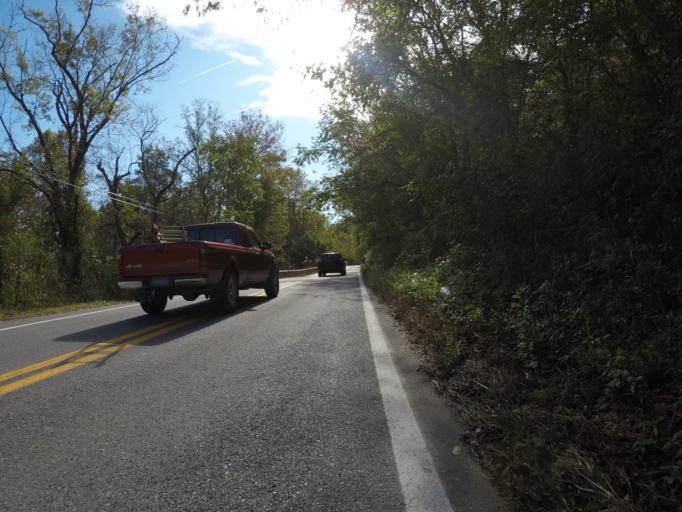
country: US
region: West Virginia
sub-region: Wayne County
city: Ceredo
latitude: 38.3708
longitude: -82.5458
